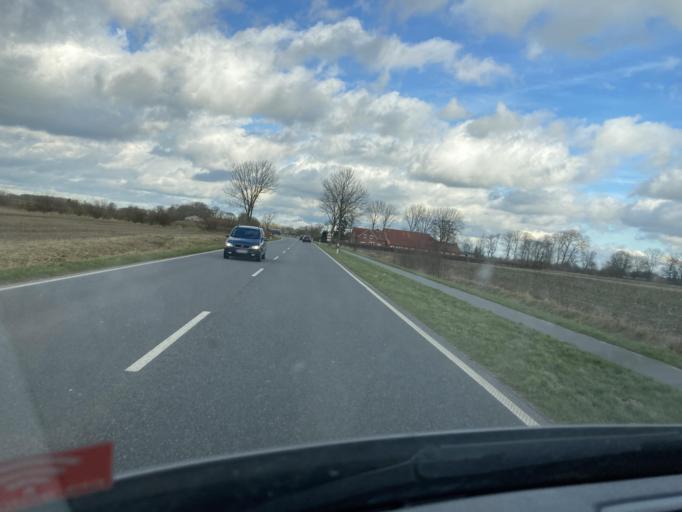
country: DE
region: Lower Saxony
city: Zetel
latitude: 53.4648
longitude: 7.9519
